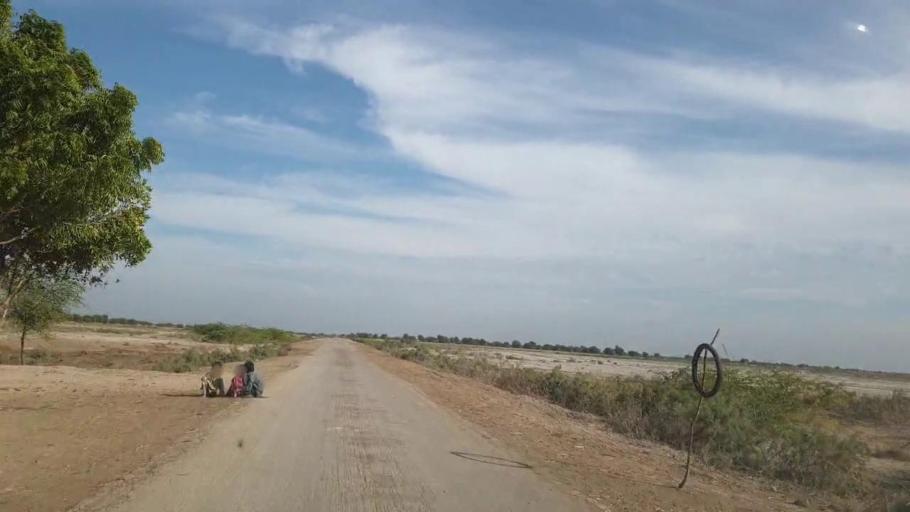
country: PK
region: Sindh
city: Pithoro
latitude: 25.6381
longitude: 69.3844
